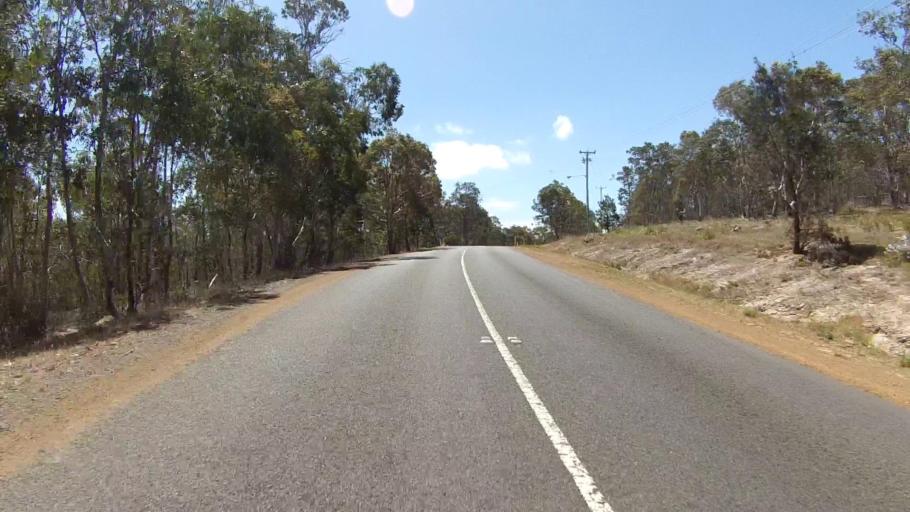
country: AU
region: Tasmania
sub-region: Clarence
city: Sandford
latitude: -42.9762
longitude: 147.4801
